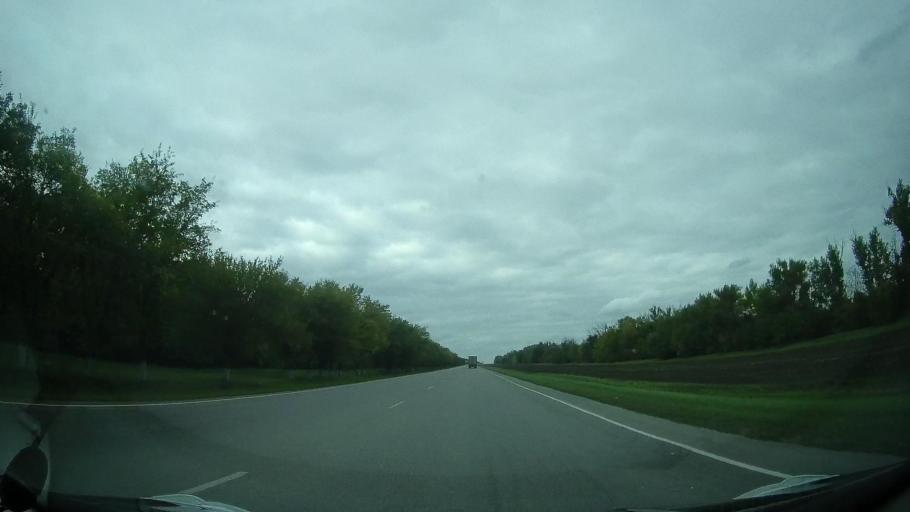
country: RU
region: Rostov
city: Yegorlykskaya
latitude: 46.6172
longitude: 40.6008
